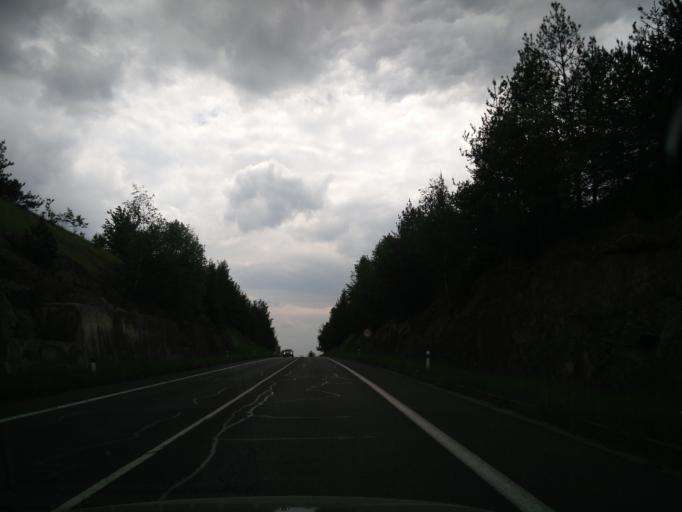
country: CZ
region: Central Bohemia
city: Milin
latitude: 49.6269
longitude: 14.0516
